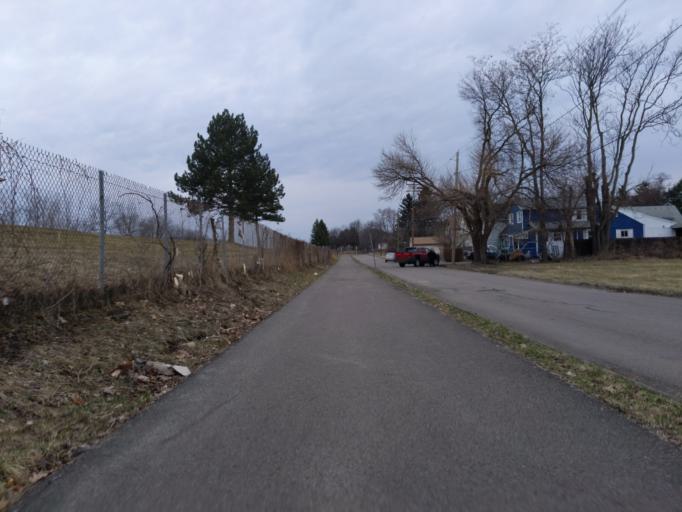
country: US
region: New York
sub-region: Chemung County
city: Elmira
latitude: 42.1084
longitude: -76.8122
